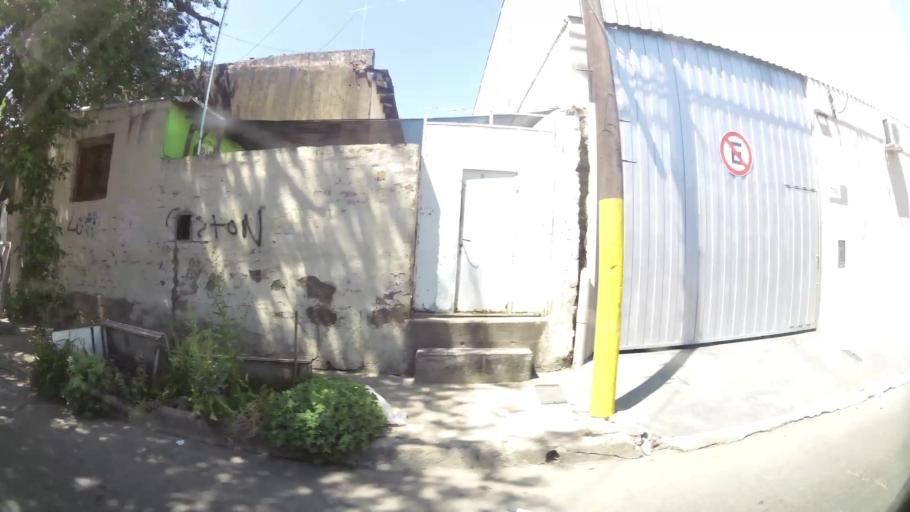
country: AR
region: Cordoba
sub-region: Departamento de Capital
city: Cordoba
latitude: -31.3976
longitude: -64.1960
